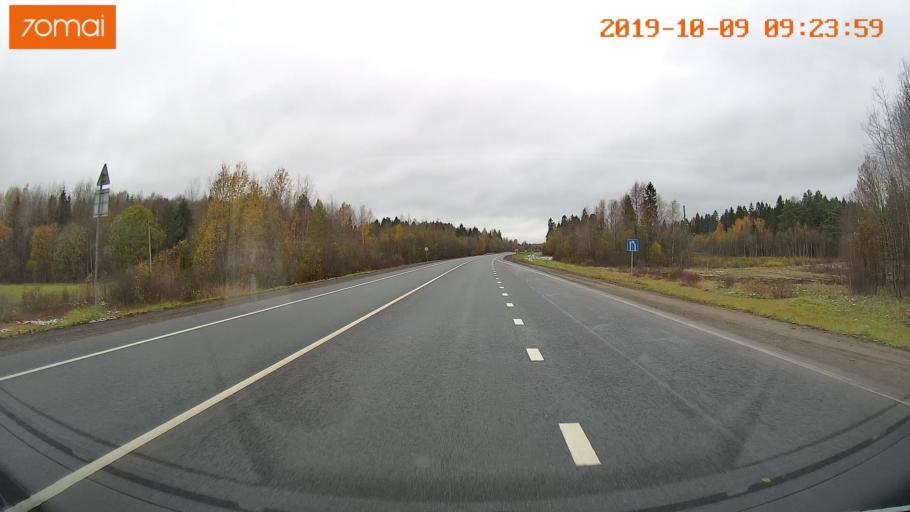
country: RU
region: Vologda
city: Vologda
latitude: 59.0744
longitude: 40.0234
